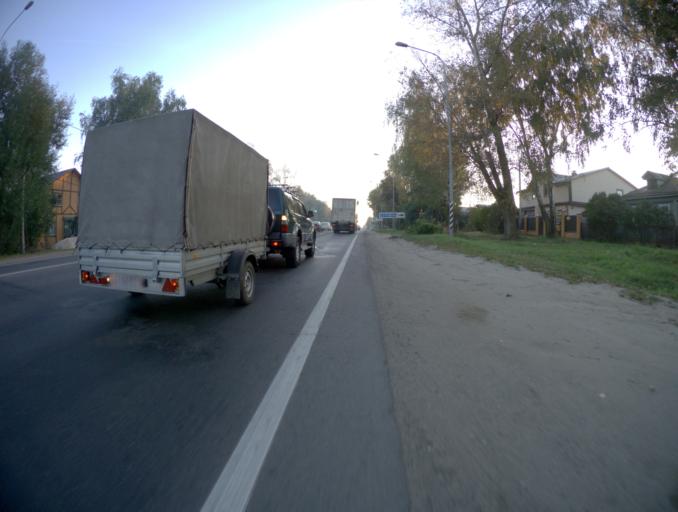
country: RU
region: Vladimir
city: Bogolyubovo
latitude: 56.1880
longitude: 40.5202
